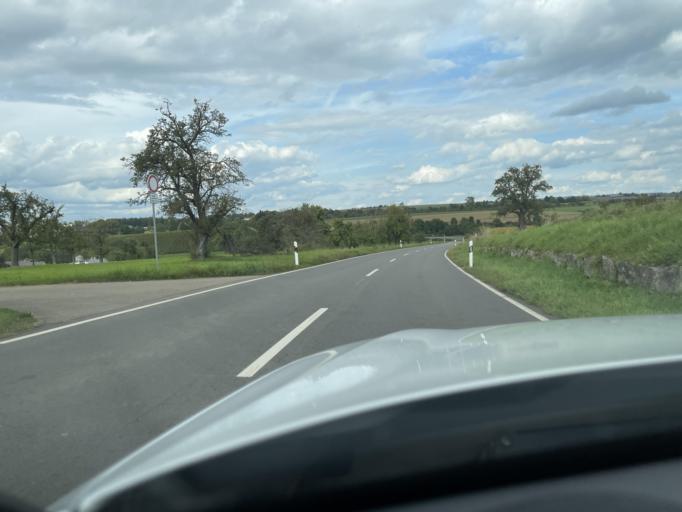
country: DE
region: Baden-Wuerttemberg
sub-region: Regierungsbezirk Stuttgart
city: Marbach am Neckar
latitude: 48.9217
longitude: 9.2666
